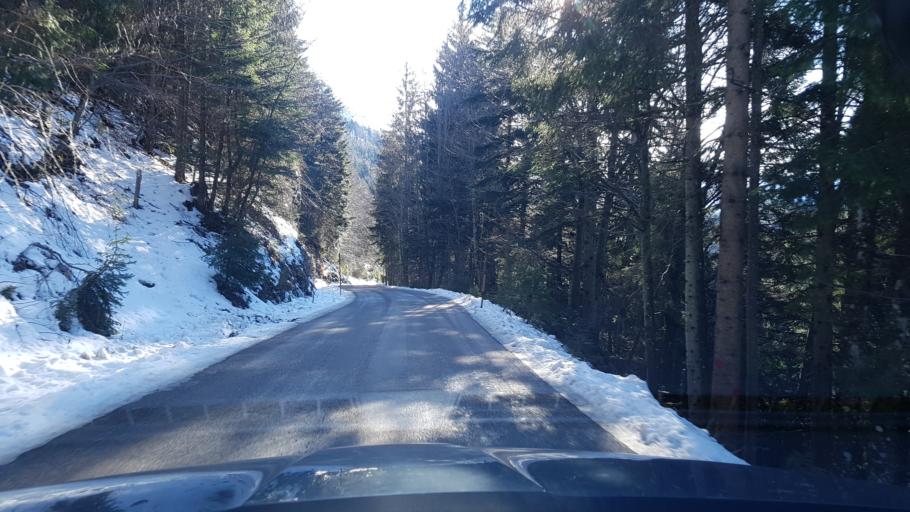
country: AT
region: Salzburg
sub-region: Politischer Bezirk Hallein
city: Scheffau am Tennengebirge
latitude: 47.6435
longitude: 13.2387
